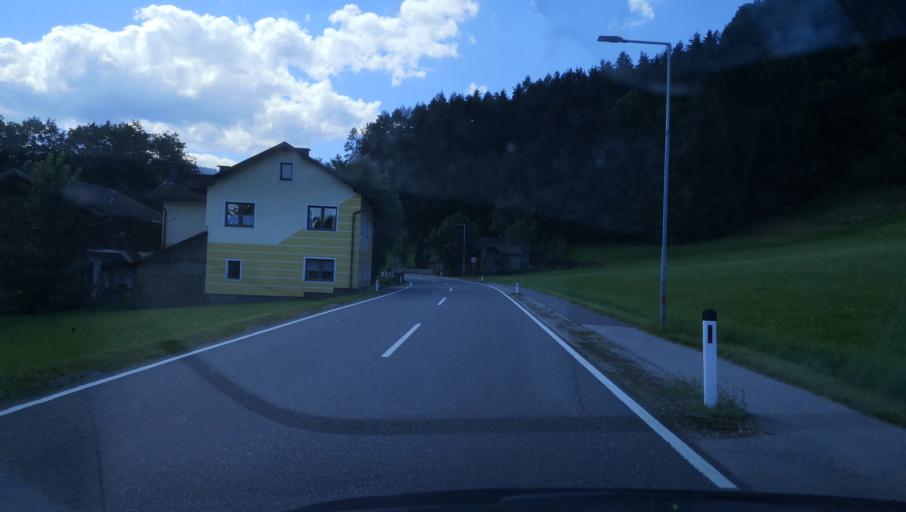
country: AT
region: Lower Austria
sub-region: Politischer Bezirk Scheibbs
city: Gresten
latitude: 47.9696
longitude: 15.0205
